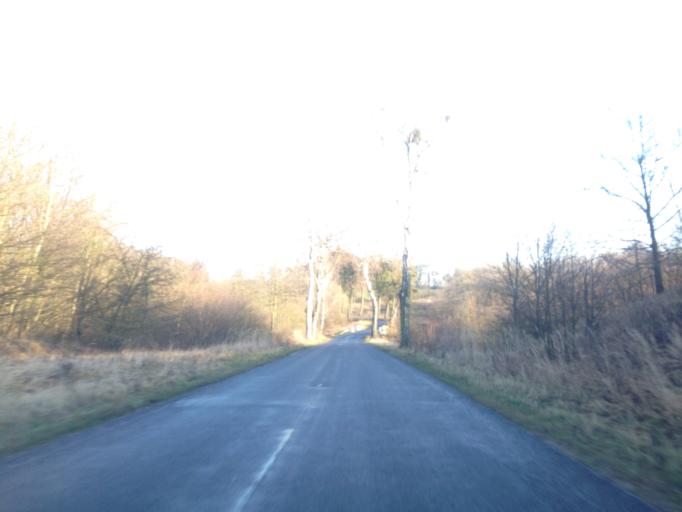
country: PL
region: Kujawsko-Pomorskie
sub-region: Powiat grudziadzki
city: Swiecie nad Osa
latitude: 53.4477
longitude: 19.1336
